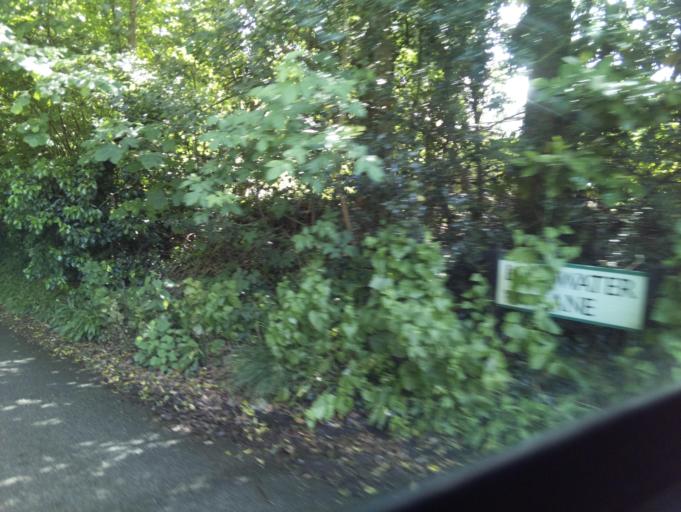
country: GB
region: England
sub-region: Hertfordshire
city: Chorleywood
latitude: 51.6573
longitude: -0.4755
